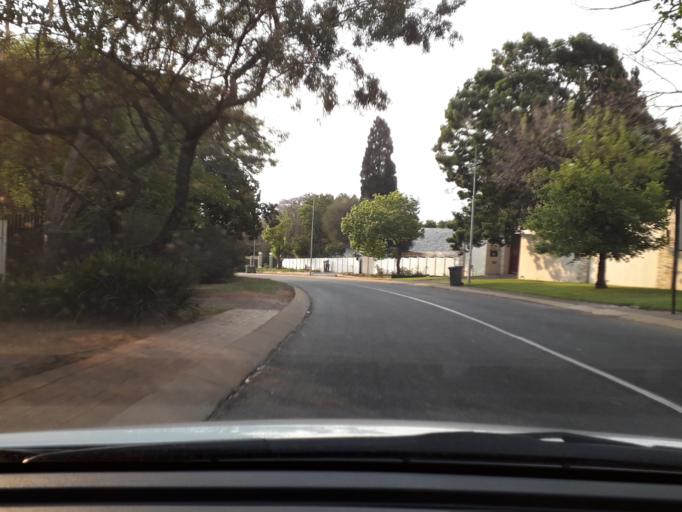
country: ZA
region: Gauteng
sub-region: City of Johannesburg Metropolitan Municipality
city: Modderfontein
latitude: -26.0736
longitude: 28.0751
